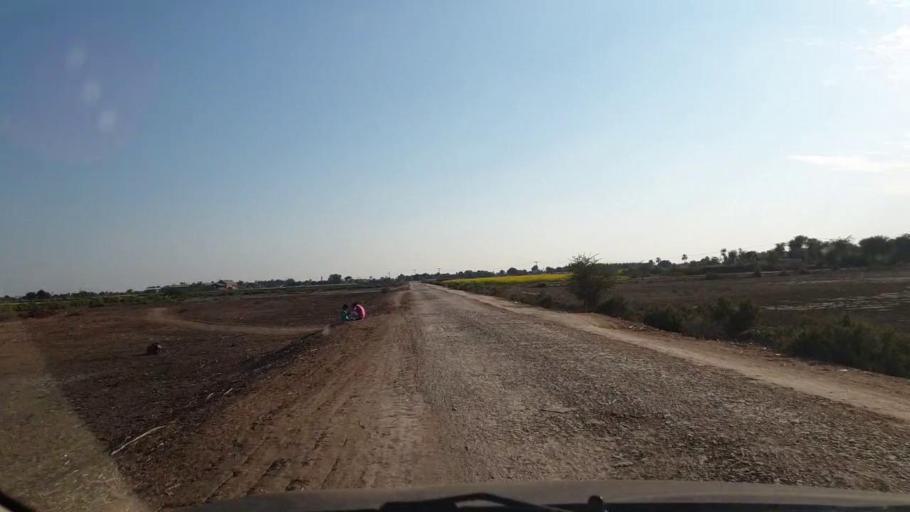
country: PK
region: Sindh
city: Jhol
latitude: 25.9579
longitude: 68.8615
